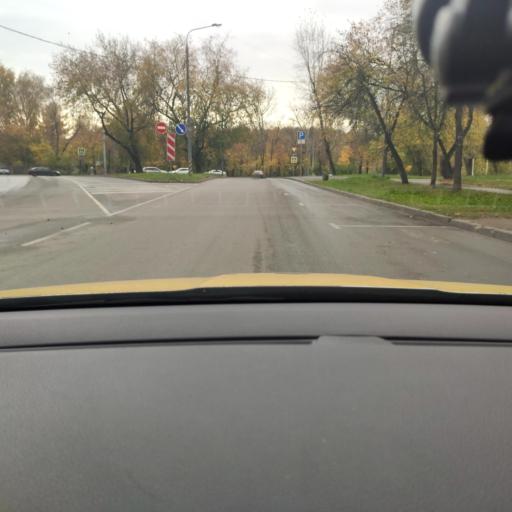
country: RU
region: Moscow
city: Metrogorodok
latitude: 55.7908
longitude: 37.7697
